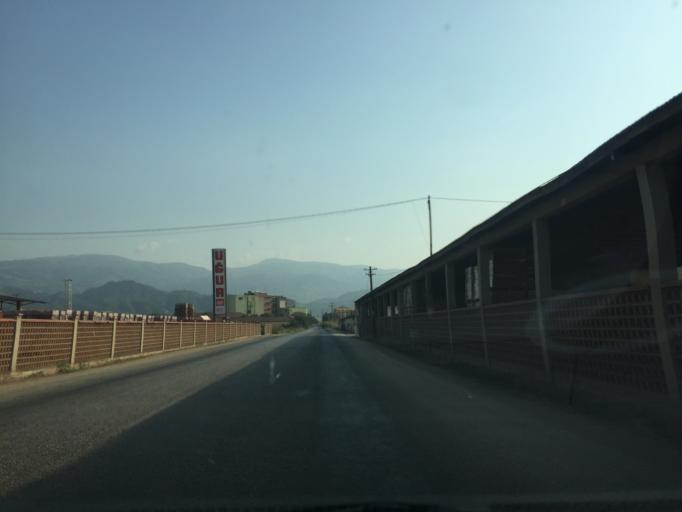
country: TR
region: Manisa
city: Salihli
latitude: 38.4988
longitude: 28.1836
